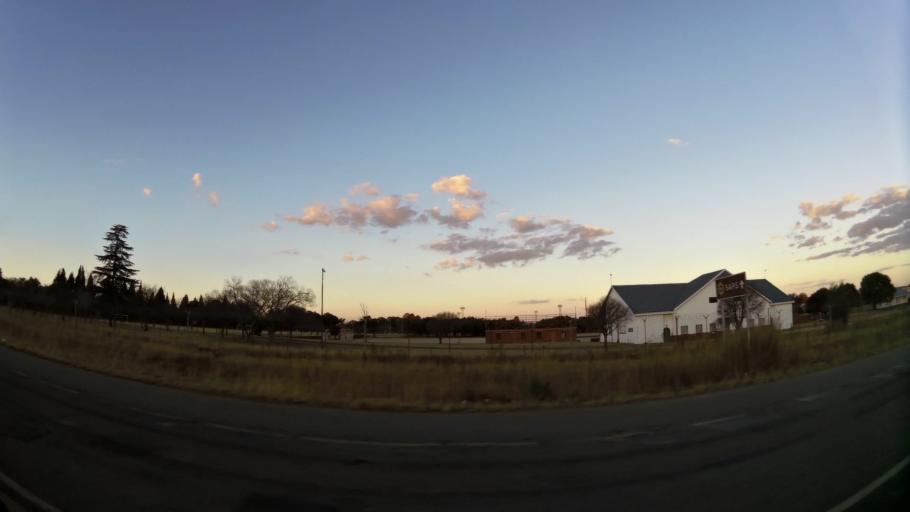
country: ZA
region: North-West
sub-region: Dr Kenneth Kaunda District Municipality
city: Potchefstroom
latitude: -26.6876
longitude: 27.0770
